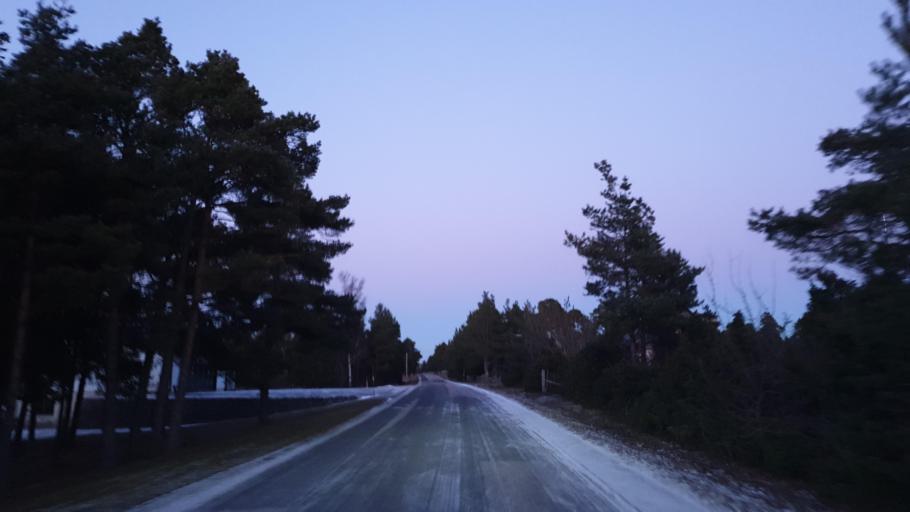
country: SE
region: Gotland
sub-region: Gotland
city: Slite
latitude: 57.4120
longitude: 18.8104
